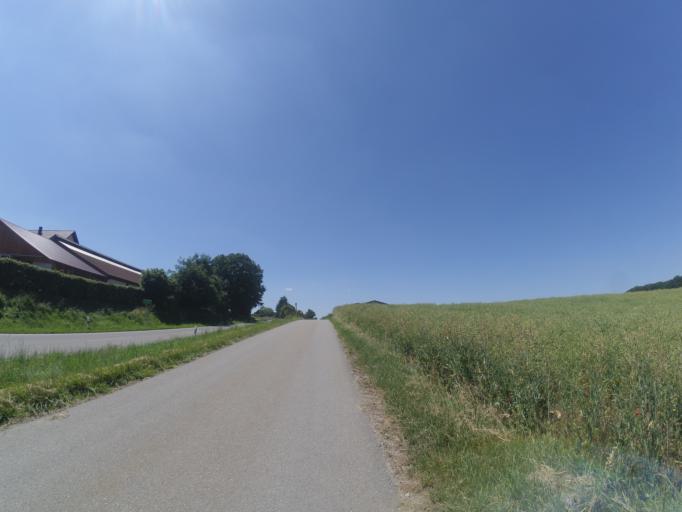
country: DE
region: Baden-Wuerttemberg
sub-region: Tuebingen Region
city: Aulendorf
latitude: 47.9308
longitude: 9.6710
